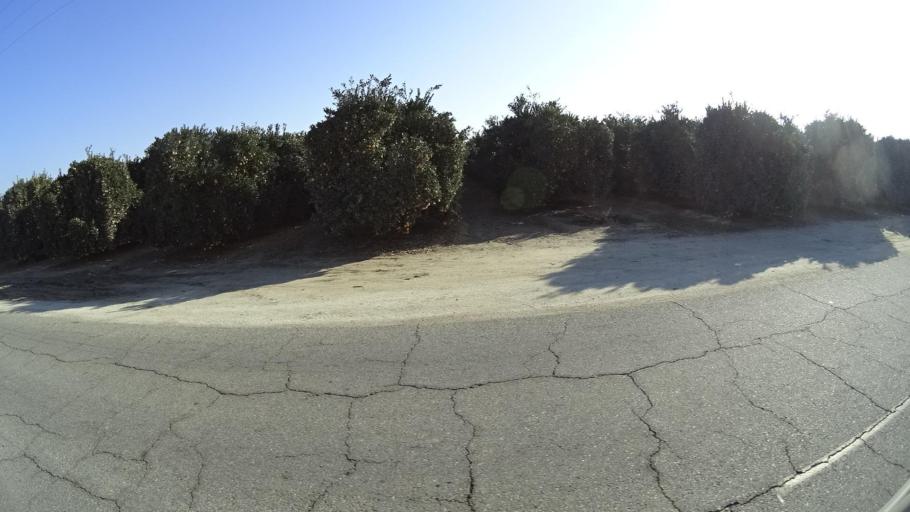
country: US
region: California
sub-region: Tulare County
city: Richgrove
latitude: 35.7866
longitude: -119.1697
